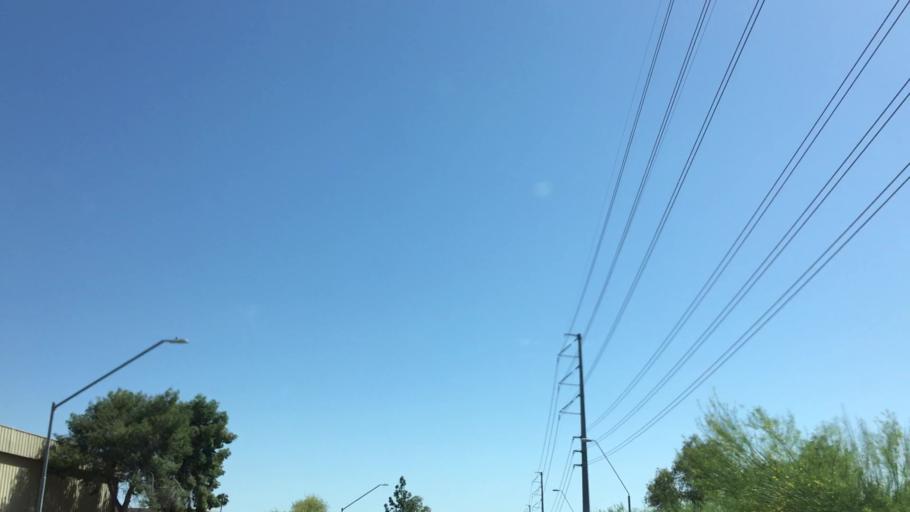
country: US
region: Arizona
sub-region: Maricopa County
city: Peoria
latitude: 33.5879
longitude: -112.2029
